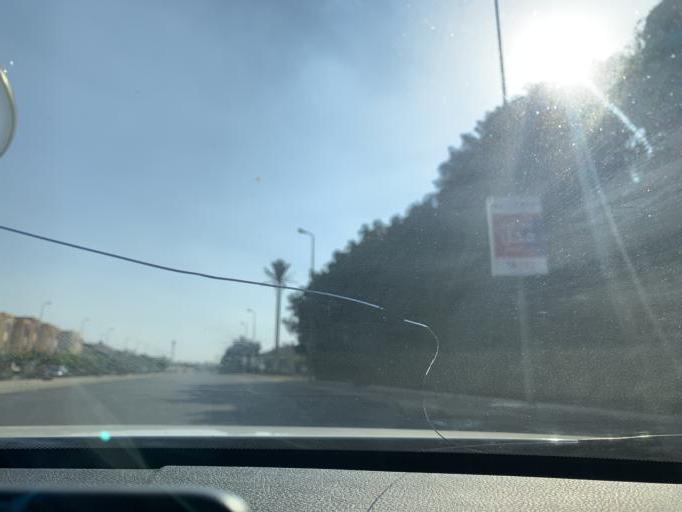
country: EG
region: Muhafazat al Qalyubiyah
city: Al Khankah
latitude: 30.0175
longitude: 31.4860
